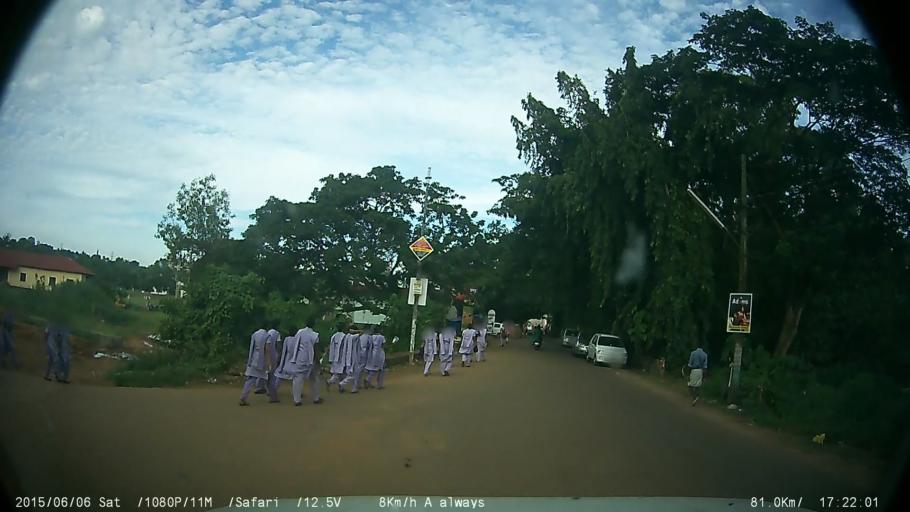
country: IN
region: Kerala
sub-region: Pattanamtitta
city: Tiruvalla
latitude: 9.3839
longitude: 76.5779
